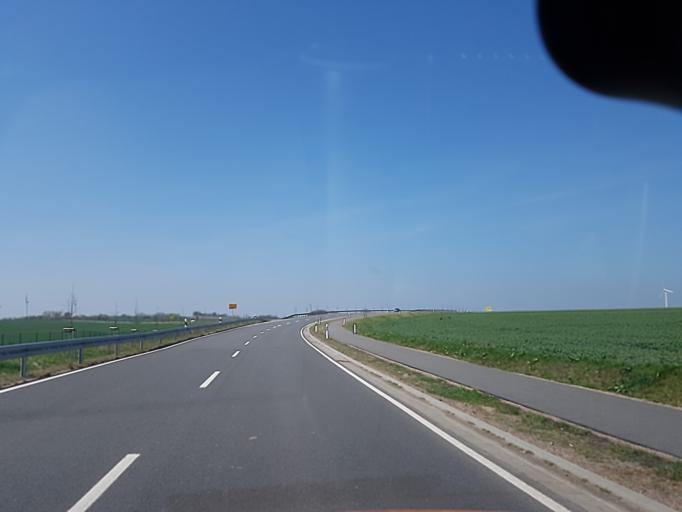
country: DE
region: Saxony
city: Ostrau
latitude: 51.2362
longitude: 12.8497
